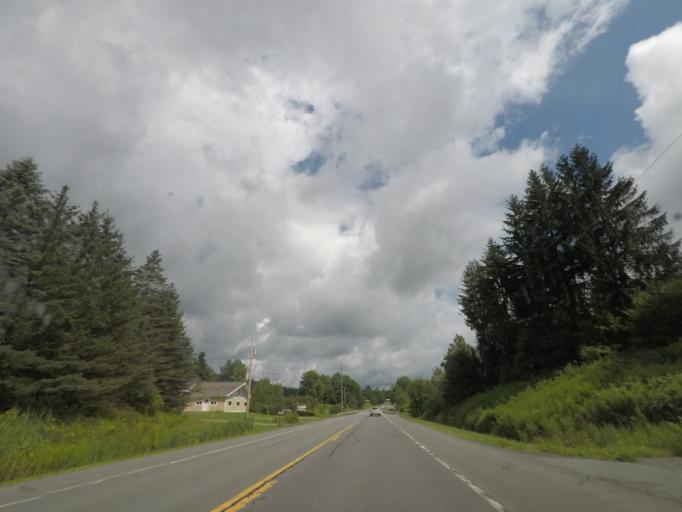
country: US
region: Massachusetts
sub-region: Berkshire County
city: Lanesborough
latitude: 42.5554
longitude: -73.3745
